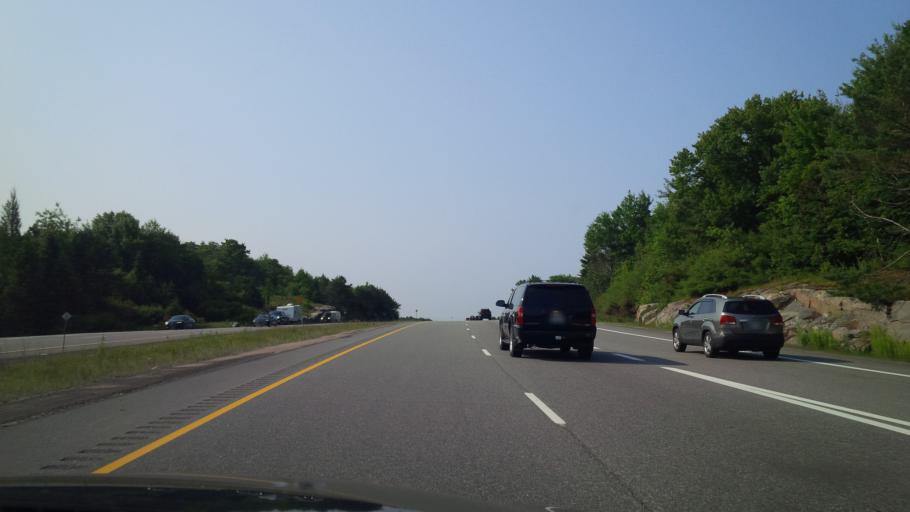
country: CA
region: Ontario
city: Bracebridge
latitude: 45.0819
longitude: -79.2967
